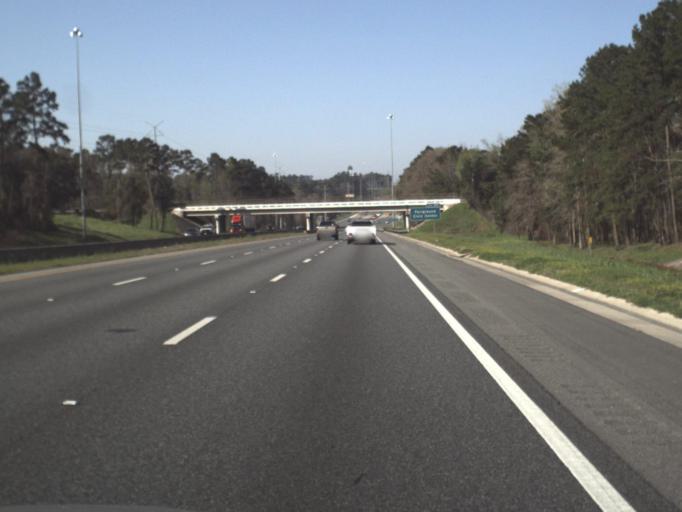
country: US
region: Florida
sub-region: Leon County
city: Tallahassee
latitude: 30.4877
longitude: -84.2927
